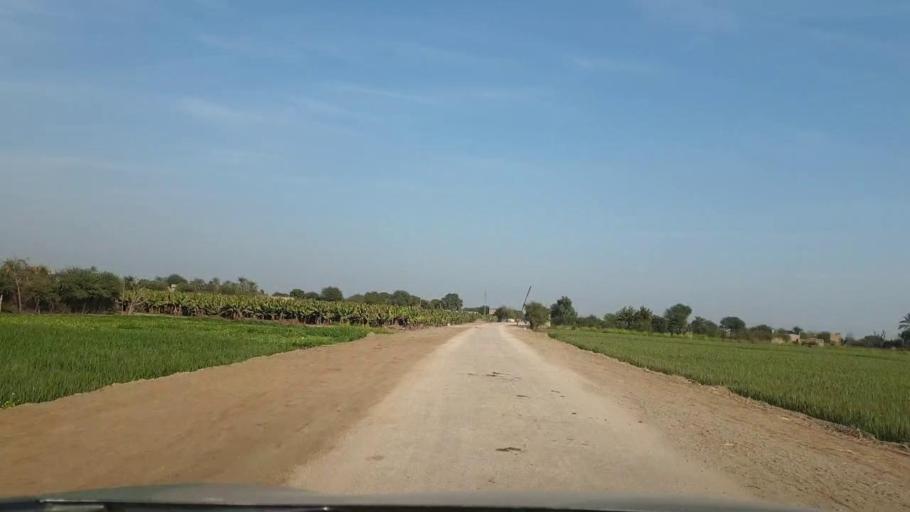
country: PK
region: Sindh
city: Berani
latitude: 25.7343
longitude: 68.8007
